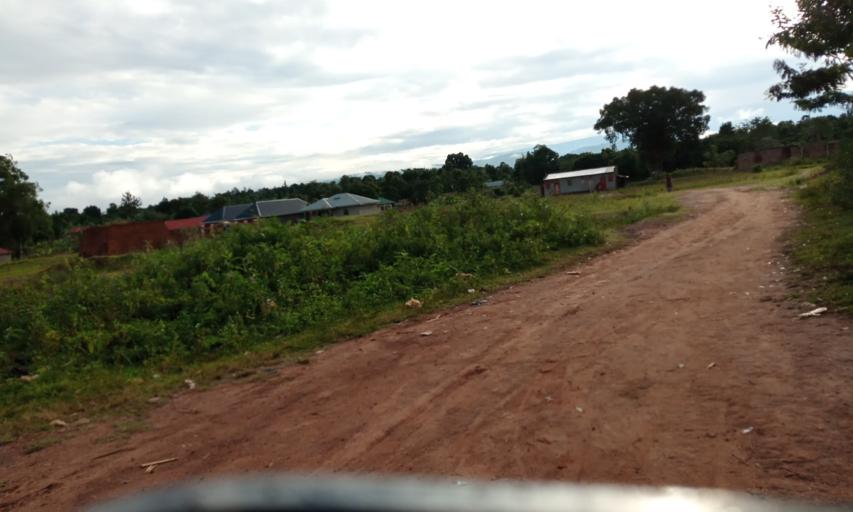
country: UG
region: Eastern Region
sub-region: Mbale District
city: Mbale
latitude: 1.1443
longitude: 34.1673
